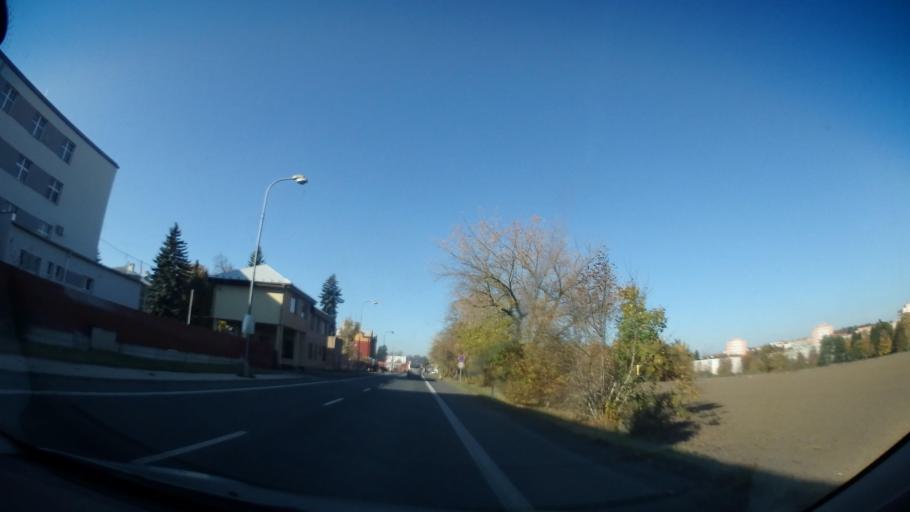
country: CZ
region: Pardubicky
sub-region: Okres Chrudim
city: Chrudim
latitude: 49.9354
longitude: 15.7984
